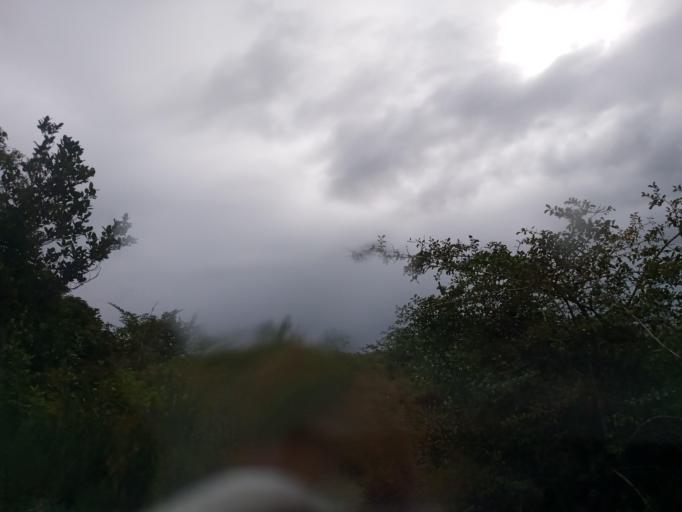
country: MG
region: Atsimo-Atsinanana
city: Vohipaho
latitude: -24.0010
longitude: 47.4042
